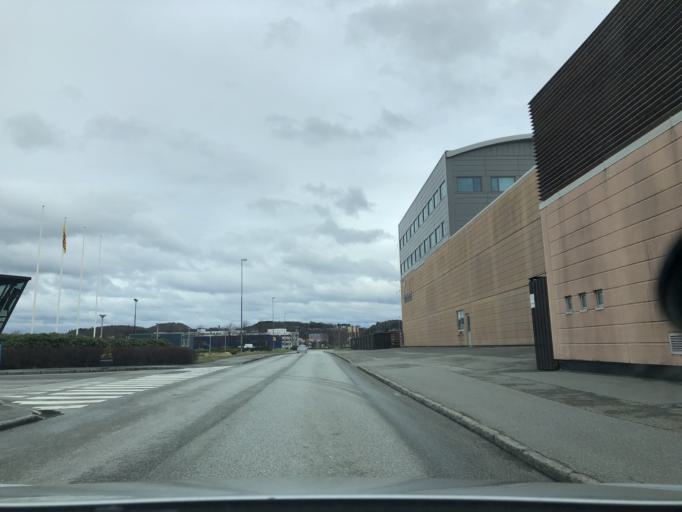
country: NO
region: Rogaland
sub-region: Sandnes
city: Sandnes
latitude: 58.8835
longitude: 5.7218
